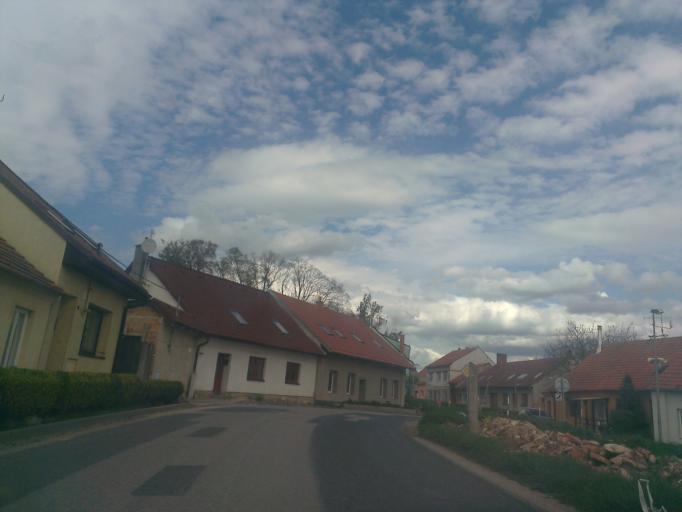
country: CZ
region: South Moravian
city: Orechov
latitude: 49.1094
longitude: 16.5140
